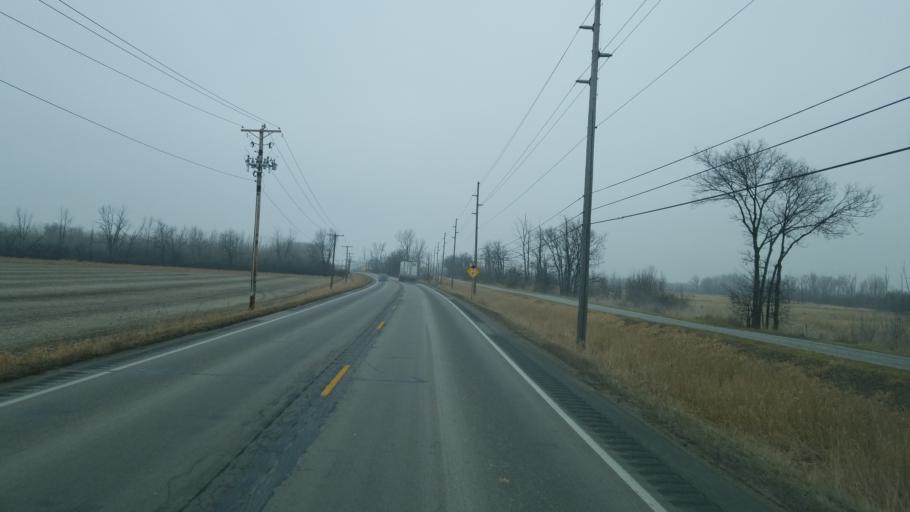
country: US
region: Indiana
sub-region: Adams County
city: Geneva
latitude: 40.5748
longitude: -84.9587
